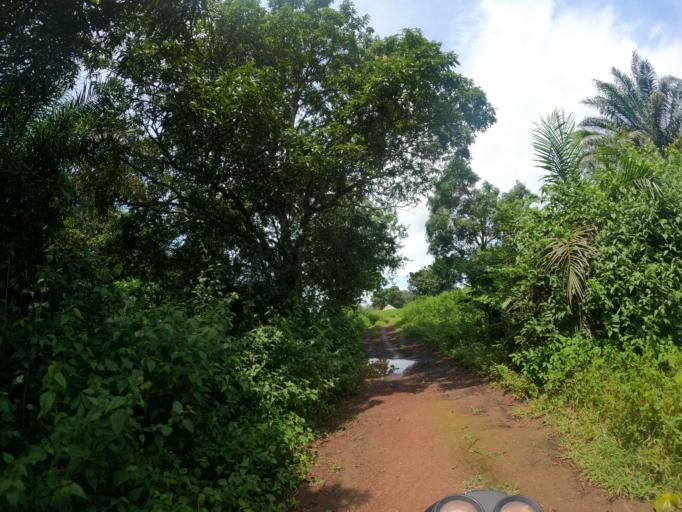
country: SL
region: Northern Province
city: Binkolo
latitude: 9.1583
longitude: -12.2098
